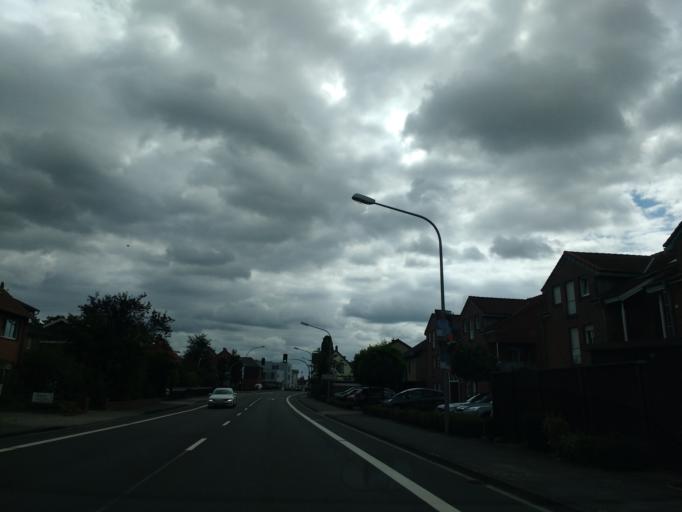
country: DE
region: North Rhine-Westphalia
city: Lengerich
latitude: 52.1941
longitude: 7.8405
